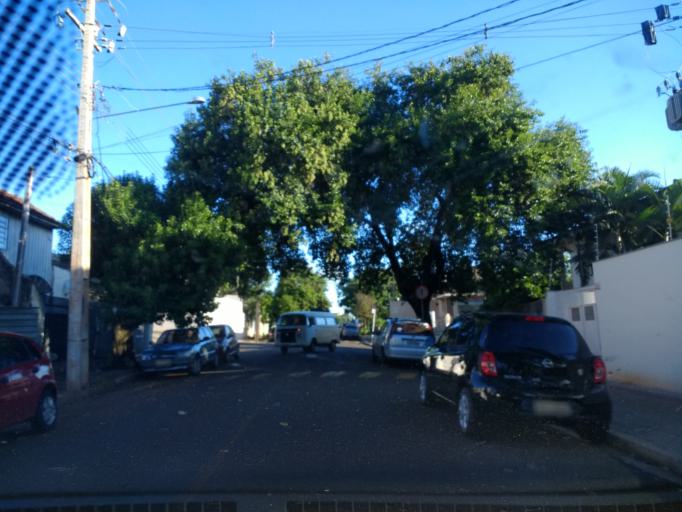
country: BR
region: Parana
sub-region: Londrina
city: Londrina
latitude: -23.3238
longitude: -51.1627
